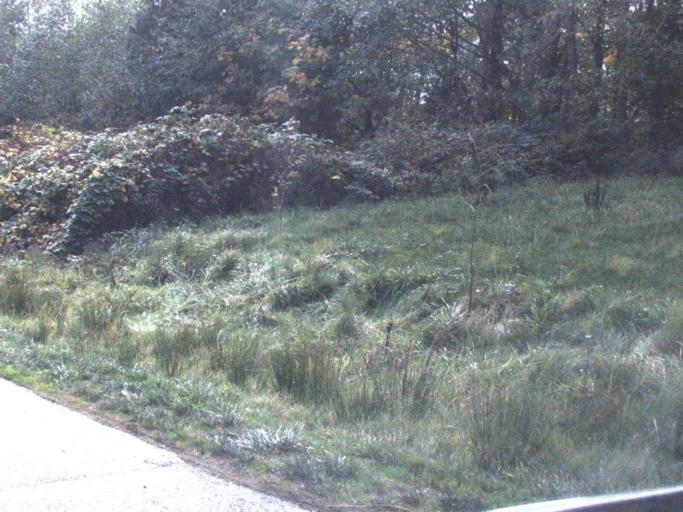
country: US
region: Washington
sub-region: Island County
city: Freeland
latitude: 48.0167
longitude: -122.5474
